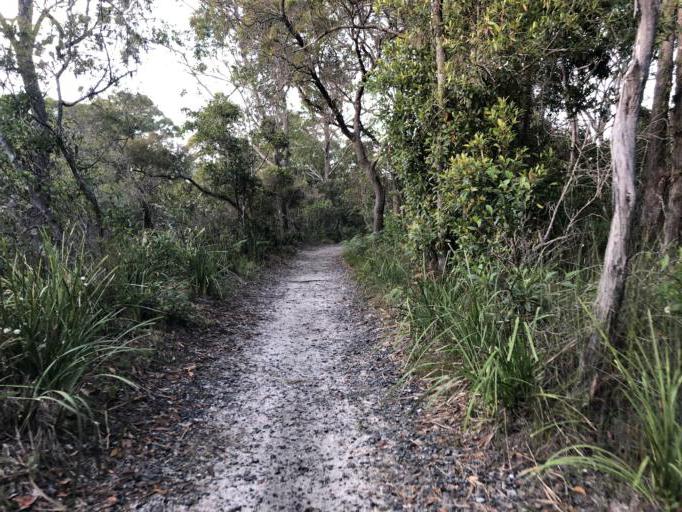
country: AU
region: New South Wales
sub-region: Coffs Harbour
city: Coffs Harbour
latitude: -30.3037
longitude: 153.1322
